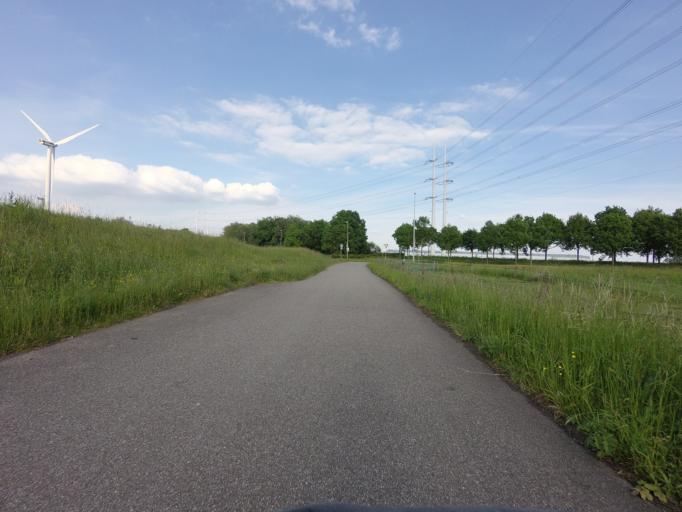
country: NL
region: South Holland
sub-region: Gemeente Zoetermeer
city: Zoetermeer
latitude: 52.0321
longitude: 4.5034
